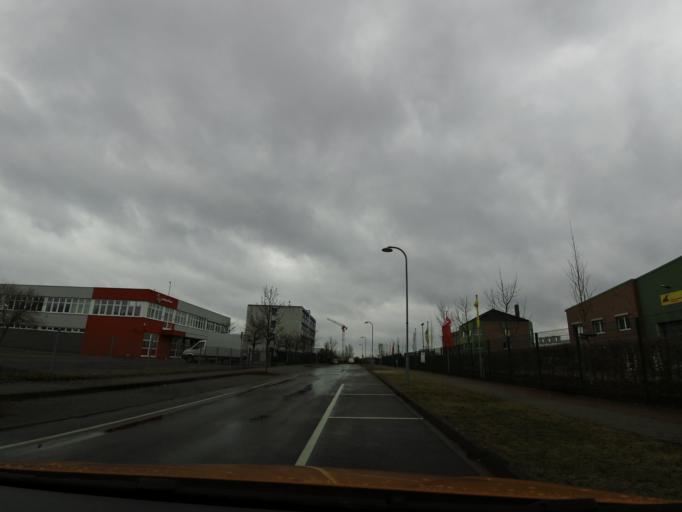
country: DE
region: Brandenburg
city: Rangsdorf
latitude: 52.3132
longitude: 13.4374
